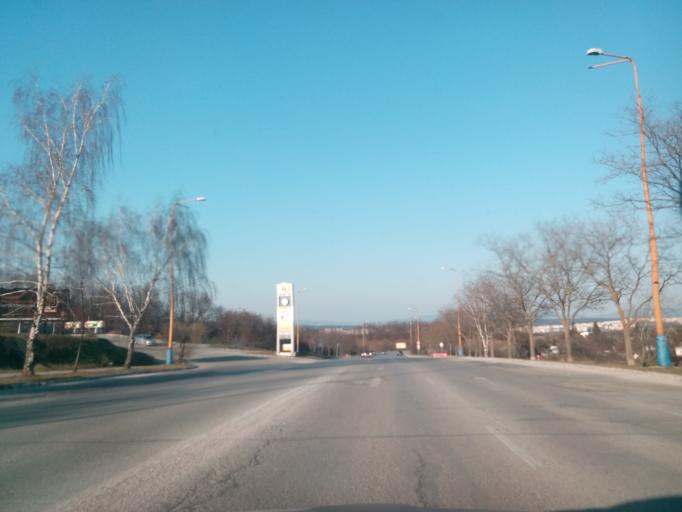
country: SK
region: Kosicky
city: Kosice
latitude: 48.7201
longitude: 21.2155
